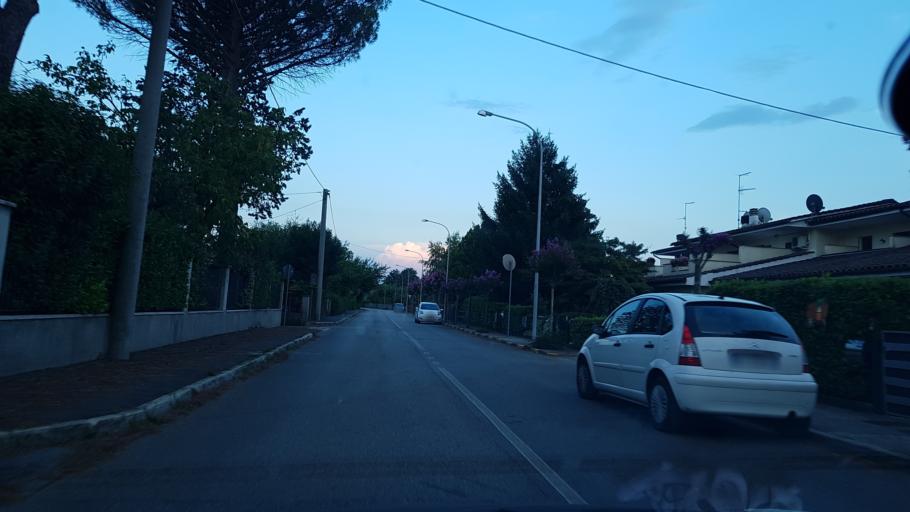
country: IT
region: Friuli Venezia Giulia
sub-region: Provincia di Gorizia
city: Capriva del Friuli
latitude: 45.9405
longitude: 13.5104
